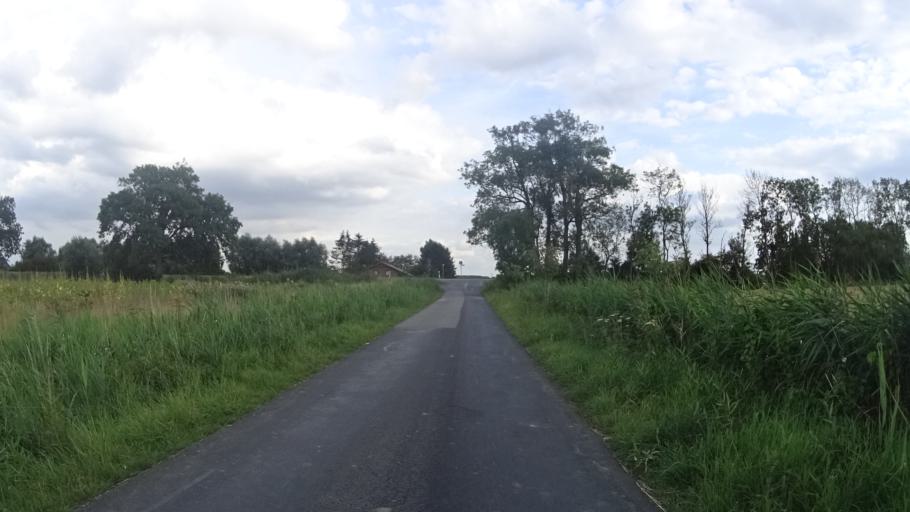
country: DE
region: Schleswig-Holstein
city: Herzhorn
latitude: 53.7776
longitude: 9.4739
